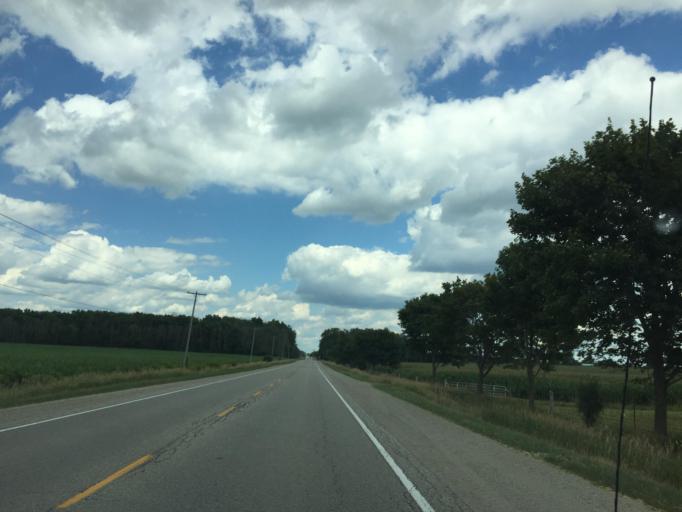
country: CA
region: Ontario
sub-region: Wellington County
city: Guelph
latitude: 43.5471
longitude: -80.3527
